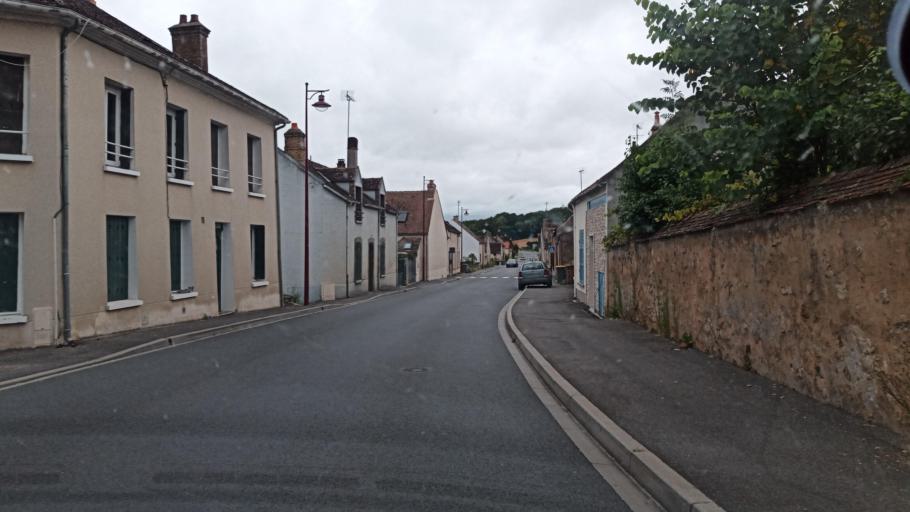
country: FR
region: Ile-de-France
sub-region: Departement de Seine-et-Marne
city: Voulx
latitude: 48.2856
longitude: 2.9603
